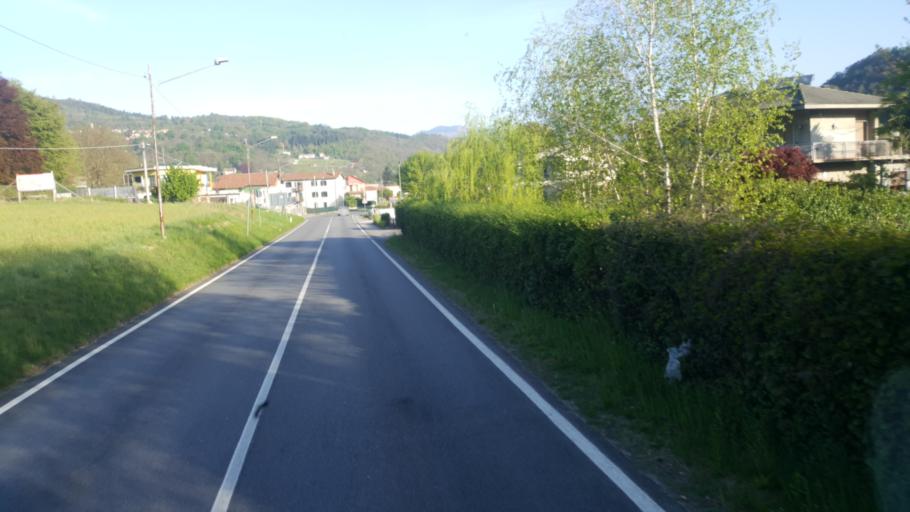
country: IT
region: Lombardy
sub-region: Provincia di Varese
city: Mesenzana
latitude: 45.9541
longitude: 8.7647
